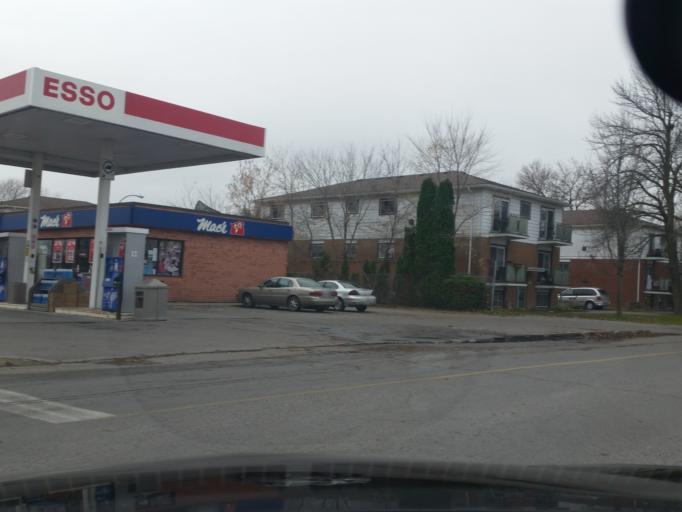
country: CA
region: Ontario
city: Quinte West
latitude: 44.1191
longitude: -77.5766
